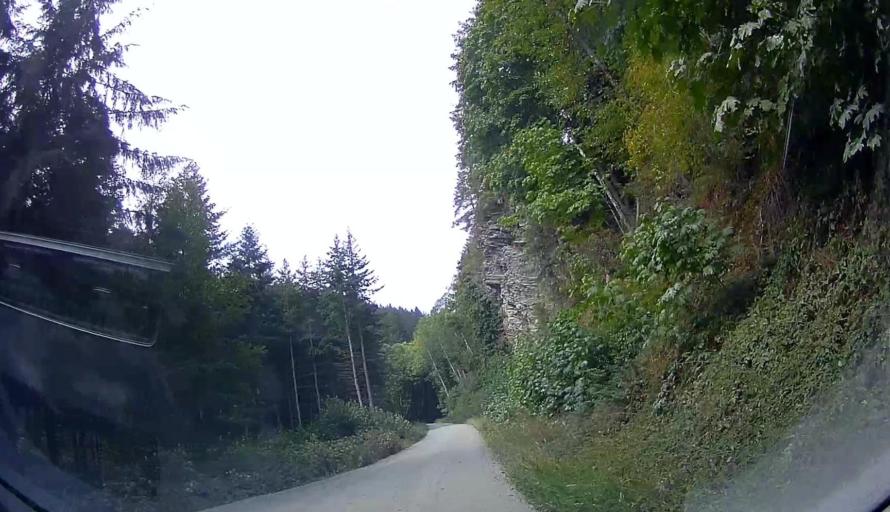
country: US
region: Washington
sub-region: Whatcom County
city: Sudden Valley
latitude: 48.6131
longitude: -122.3871
